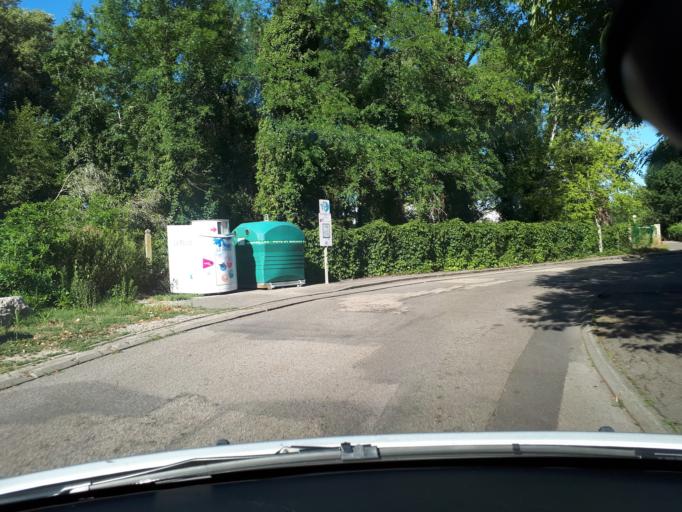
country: FR
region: Rhone-Alpes
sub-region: Departement de l'Isere
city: Bourgoin-Jallieu
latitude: 45.5901
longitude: 5.2642
